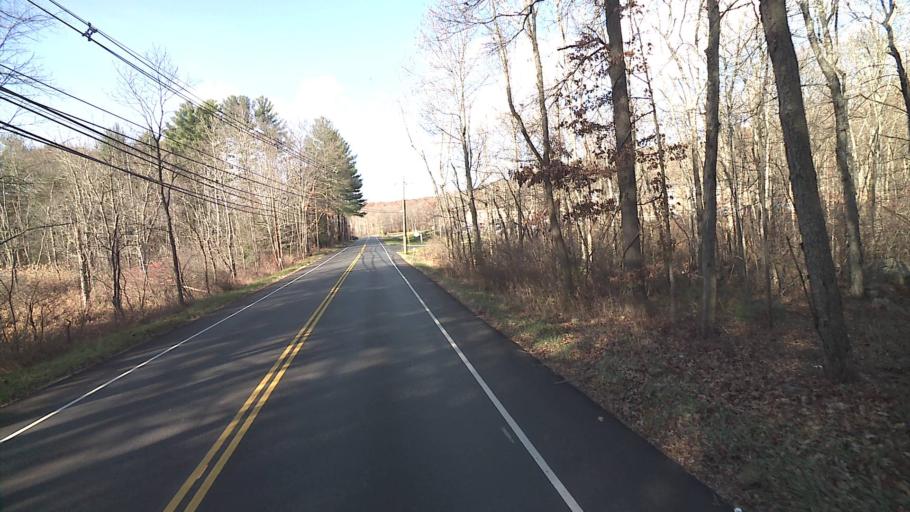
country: US
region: Connecticut
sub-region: Fairfield County
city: Georgetown
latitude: 41.3040
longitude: -73.4020
